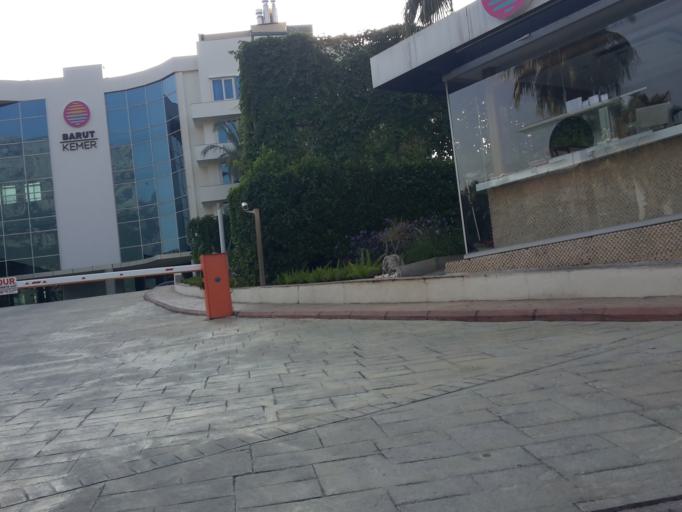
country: TR
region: Antalya
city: Kemer
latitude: 36.6095
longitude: 30.5580
